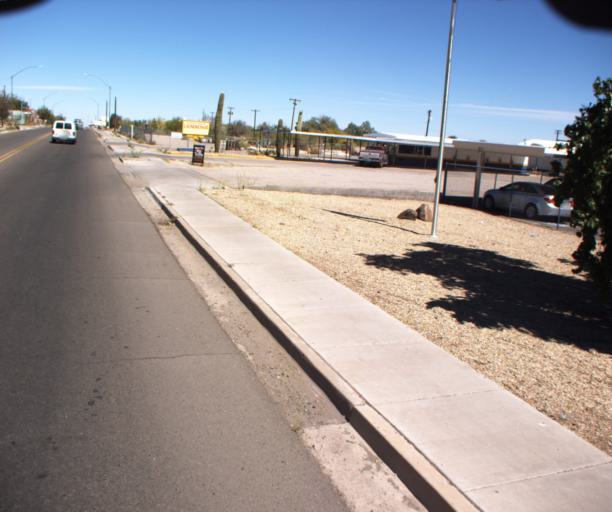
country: US
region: Arizona
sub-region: Pima County
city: Ajo
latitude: 32.3765
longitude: -112.8724
